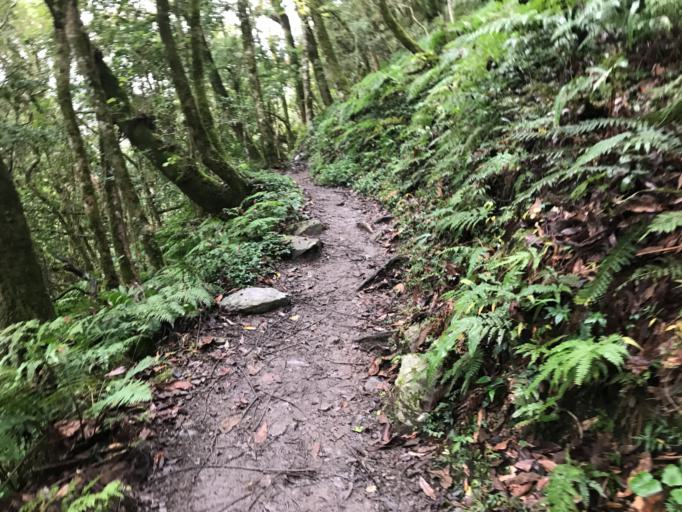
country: TW
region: Taiwan
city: Daxi
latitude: 24.5499
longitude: 121.2920
